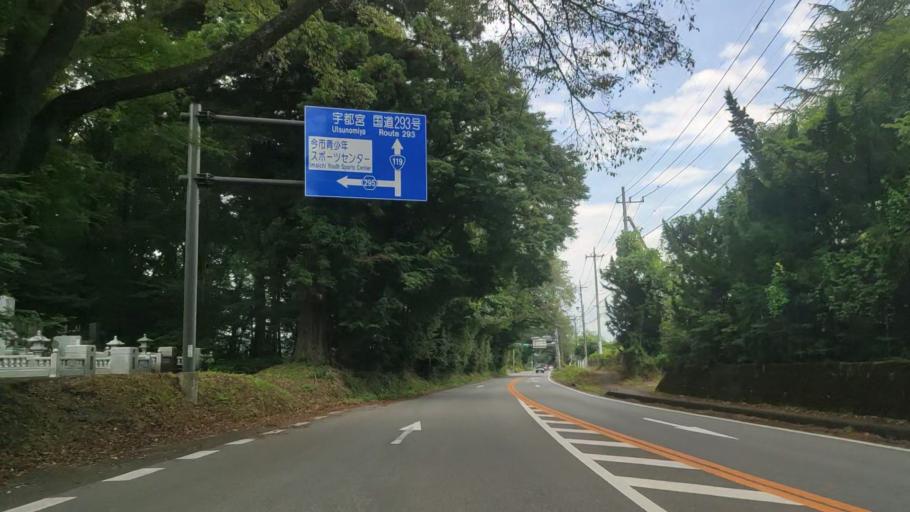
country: JP
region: Tochigi
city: Imaichi
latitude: 36.6900
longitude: 139.7672
